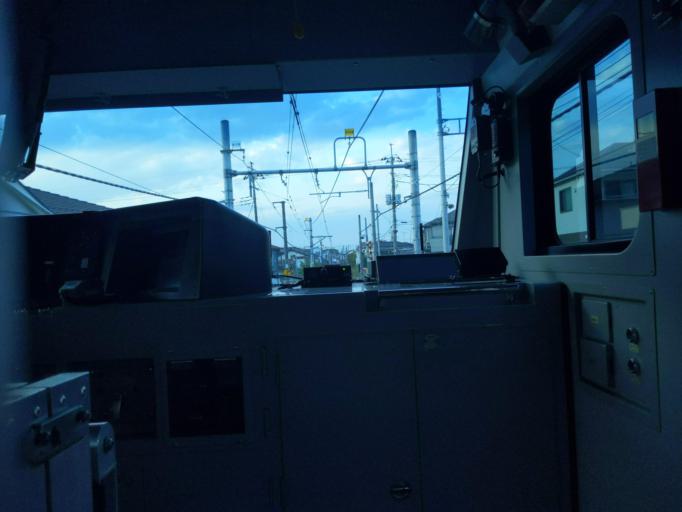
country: JP
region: Tokyo
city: Fussa
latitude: 35.7253
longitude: 139.3398
